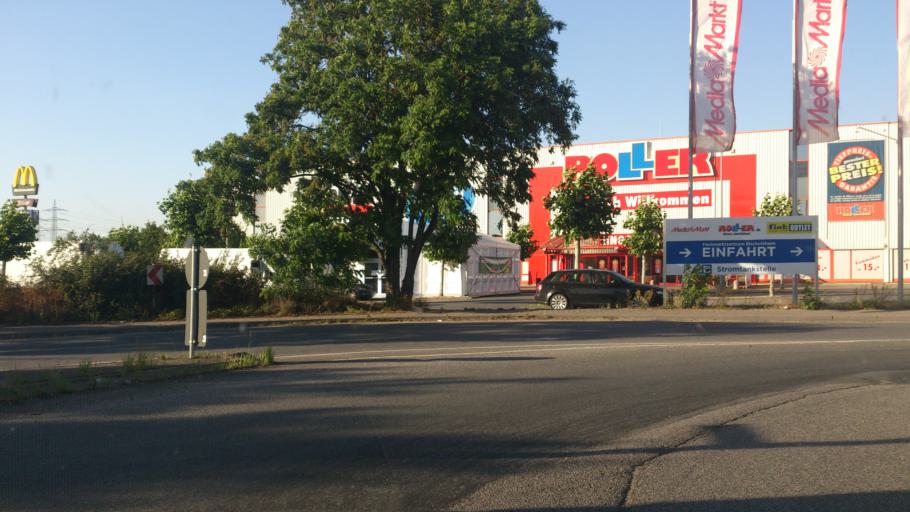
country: DE
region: Hesse
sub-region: Regierungsbezirk Darmstadt
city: Bischofsheim
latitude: 49.9752
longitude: 8.3780
